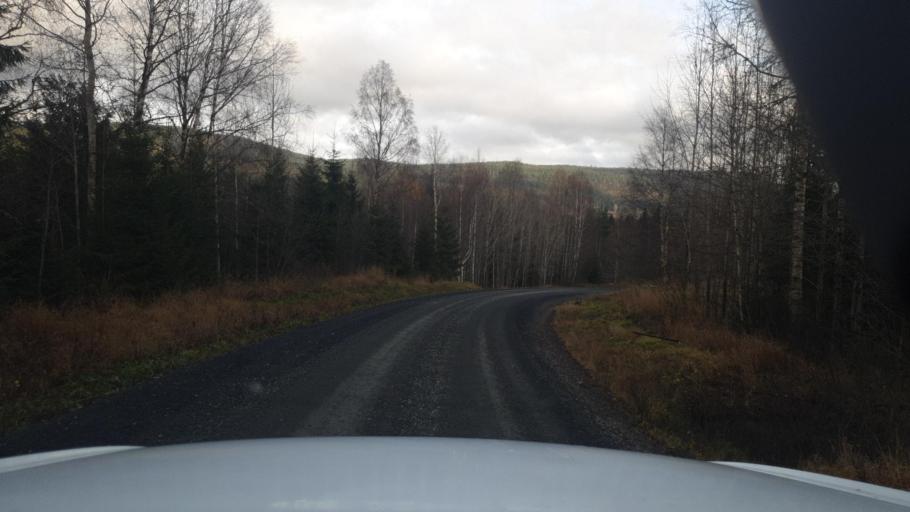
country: SE
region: Vaermland
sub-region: Torsby Kommun
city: Torsby
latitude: 60.1874
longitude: 12.6549
